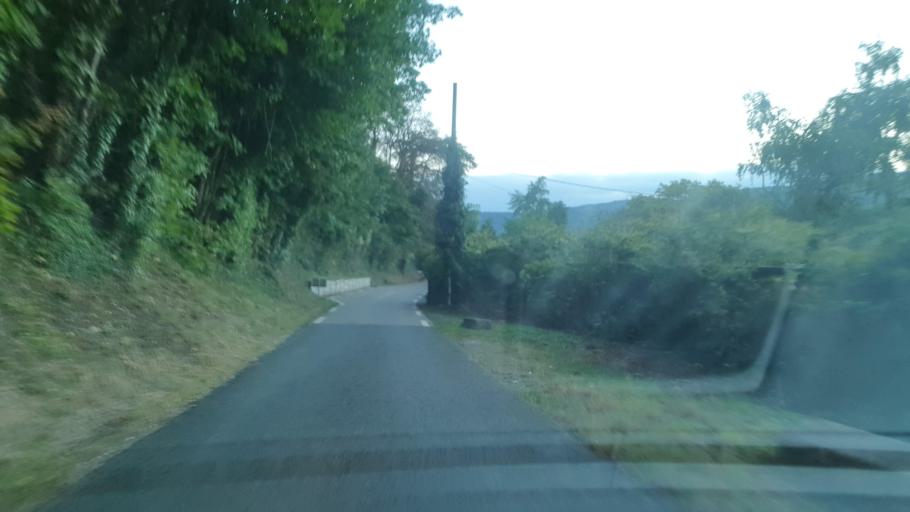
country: FR
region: Rhone-Alpes
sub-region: Departement du Rhone
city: Rochetaillee-sur-Saone
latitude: 45.8531
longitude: 4.8423
